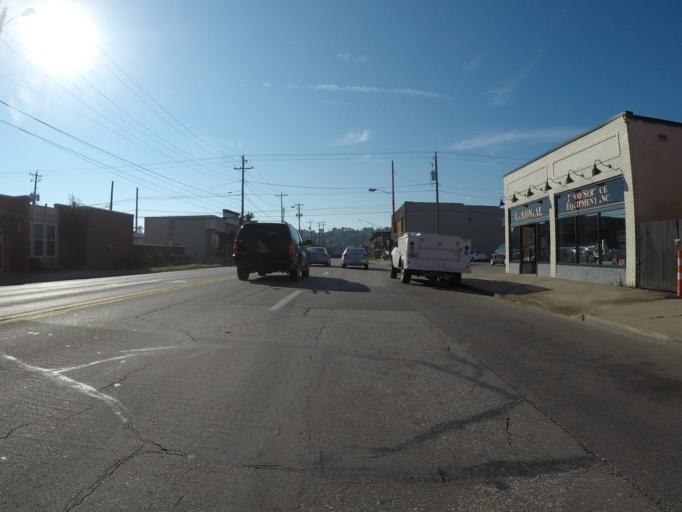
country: US
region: West Virginia
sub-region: Cabell County
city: Huntington
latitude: 38.4175
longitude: -82.4448
